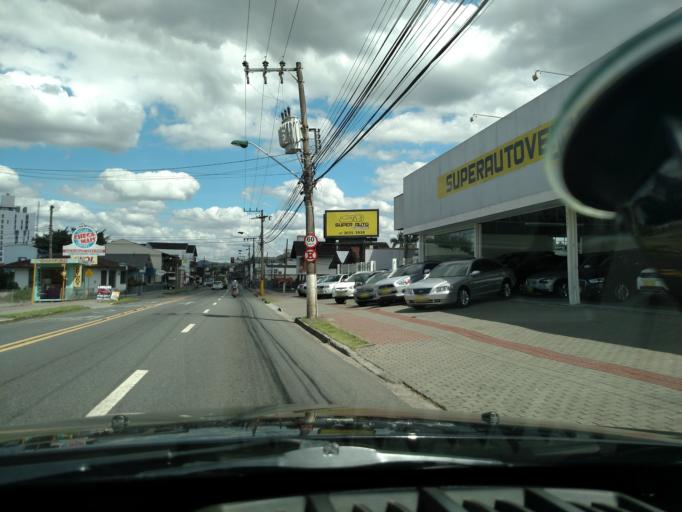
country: BR
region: Santa Catarina
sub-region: Blumenau
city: Blumenau
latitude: -26.8789
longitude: -49.0865
